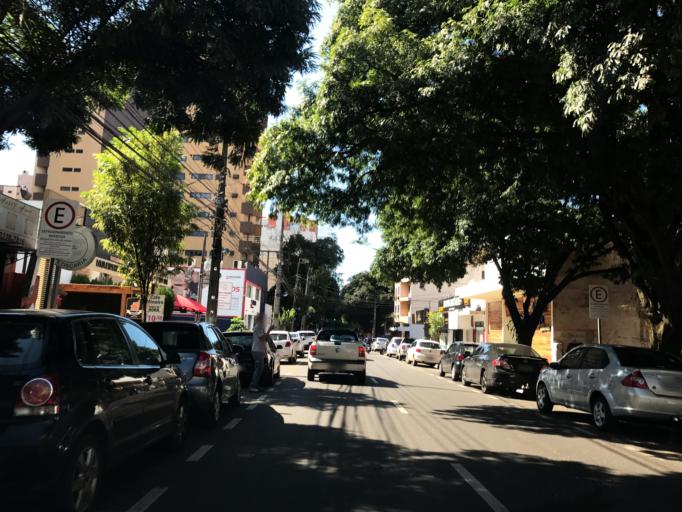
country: BR
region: Parana
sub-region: Maringa
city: Maringa
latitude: -23.4228
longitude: -51.9348
